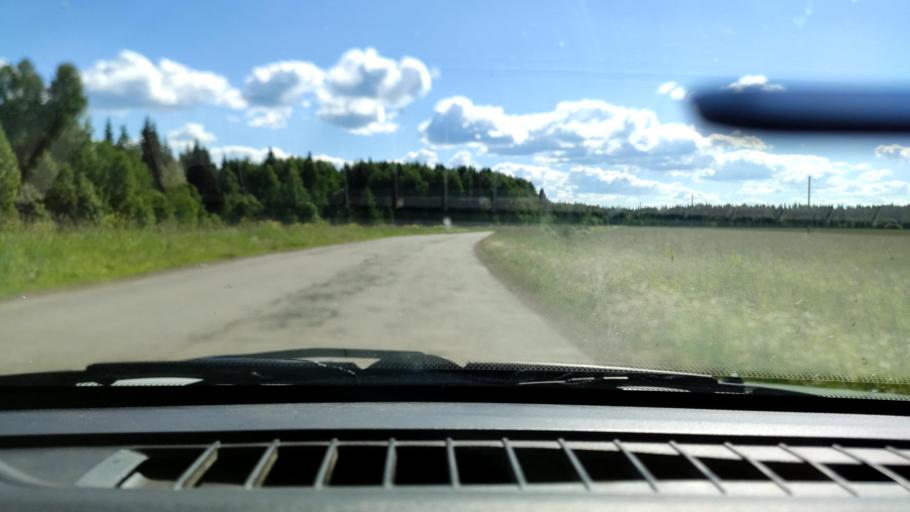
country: RU
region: Perm
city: Uinskoye
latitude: 57.1307
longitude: 56.5650
